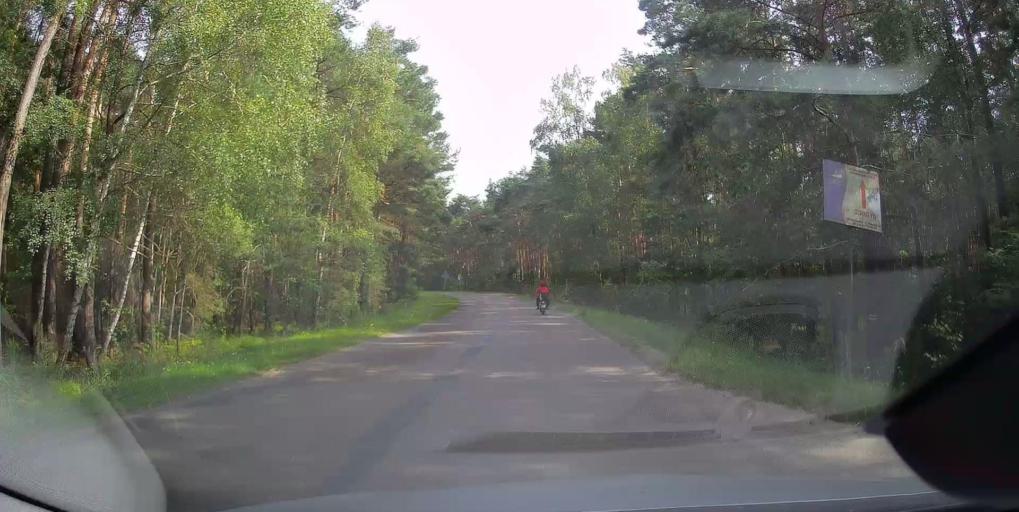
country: PL
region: Lodz Voivodeship
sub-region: Powiat tomaszowski
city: Tomaszow Mazowiecki
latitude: 51.4756
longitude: 19.9868
